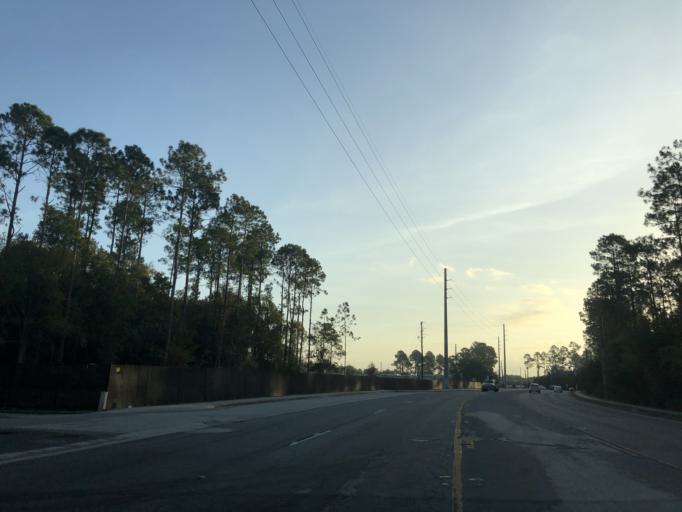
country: US
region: Florida
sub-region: Osceola County
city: Kissimmee
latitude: 28.3263
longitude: -81.4205
